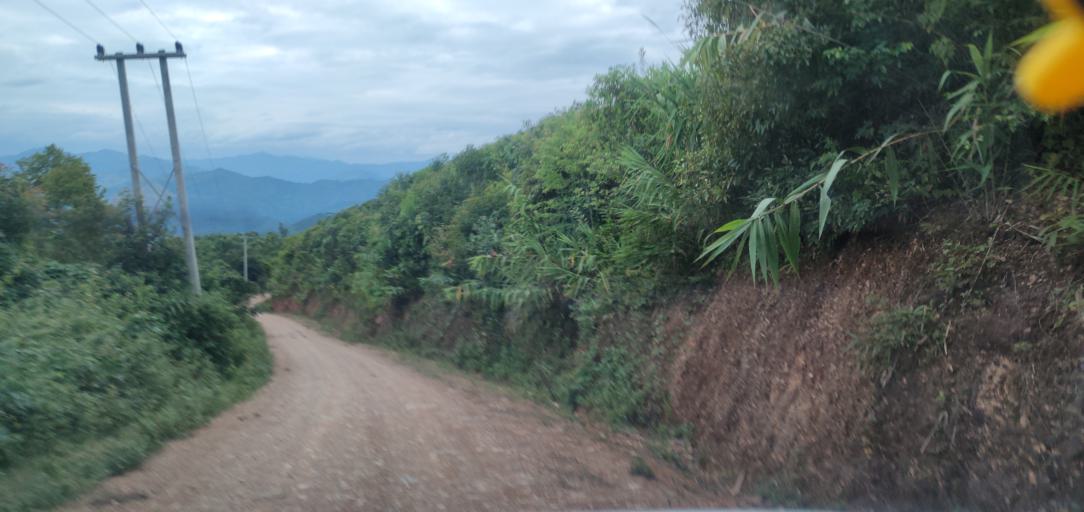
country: LA
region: Phongsali
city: Khoa
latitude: 21.1985
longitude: 102.2712
